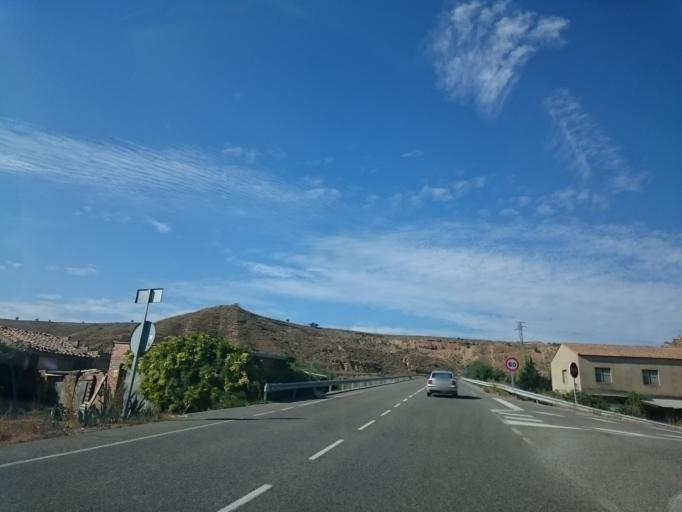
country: ES
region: Catalonia
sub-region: Provincia de Lleida
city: Alguaire
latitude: 41.7324
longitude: 0.5831
